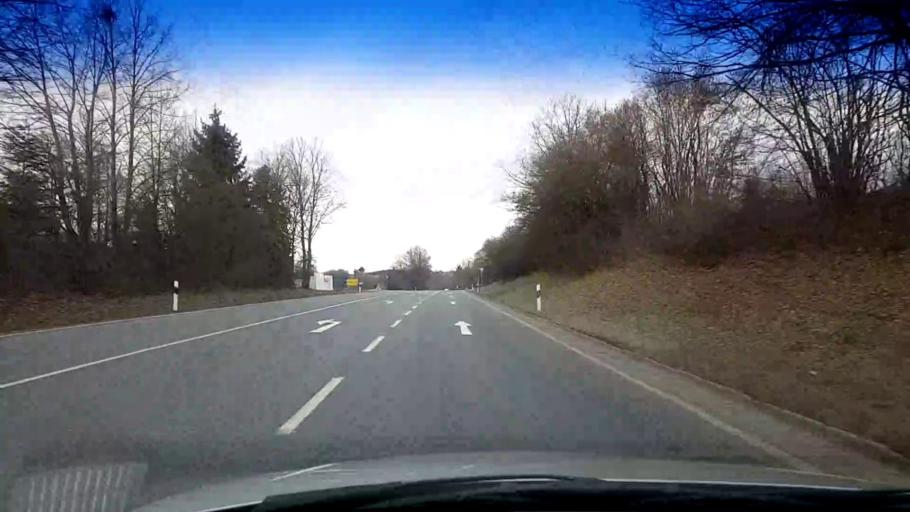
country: DE
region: Bavaria
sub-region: Upper Franconia
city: Kulmbach
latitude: 50.0740
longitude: 11.4699
